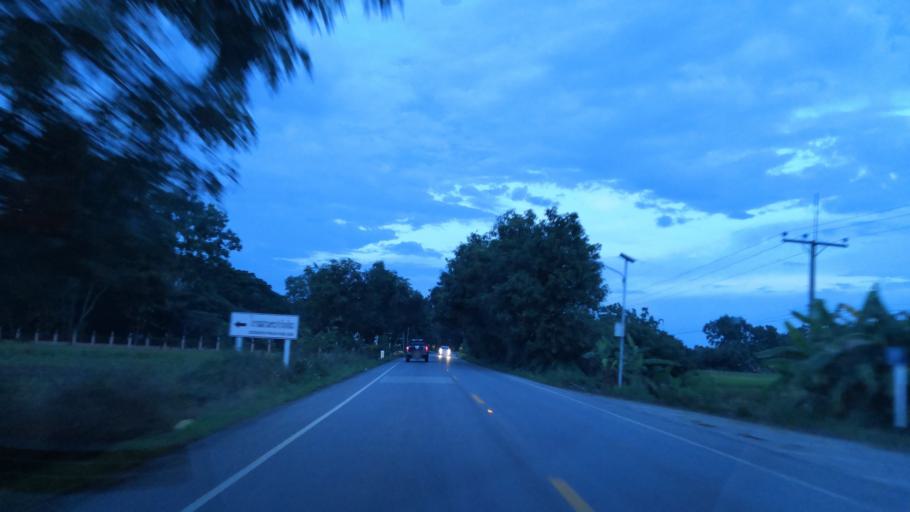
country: TH
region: Chiang Rai
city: Wiang Chai
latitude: 19.9689
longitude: 99.9650
